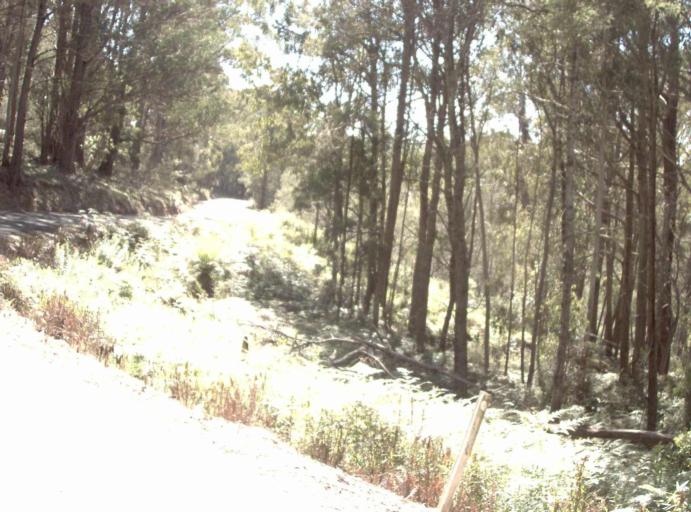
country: AU
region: New South Wales
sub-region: Bombala
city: Bombala
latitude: -37.0680
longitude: 148.7902
